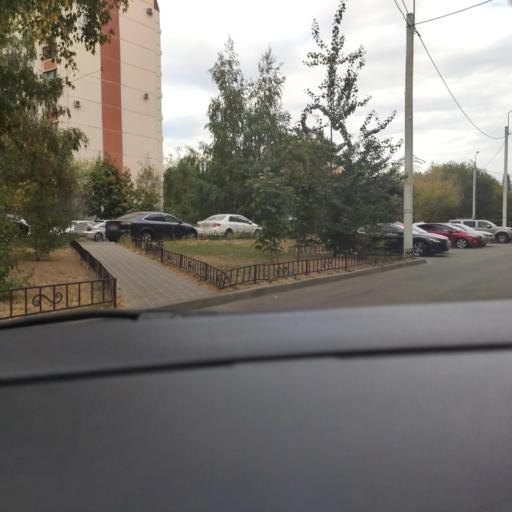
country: RU
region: Voronezj
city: Voronezh
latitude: 51.7044
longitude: 39.1900
